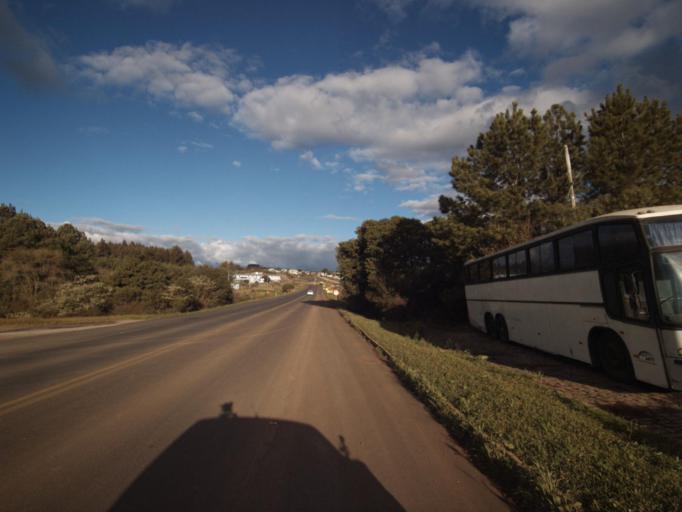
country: BR
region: Santa Catarina
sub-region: Campos Novos
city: Campos Novos
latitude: -27.3831
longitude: -51.2381
